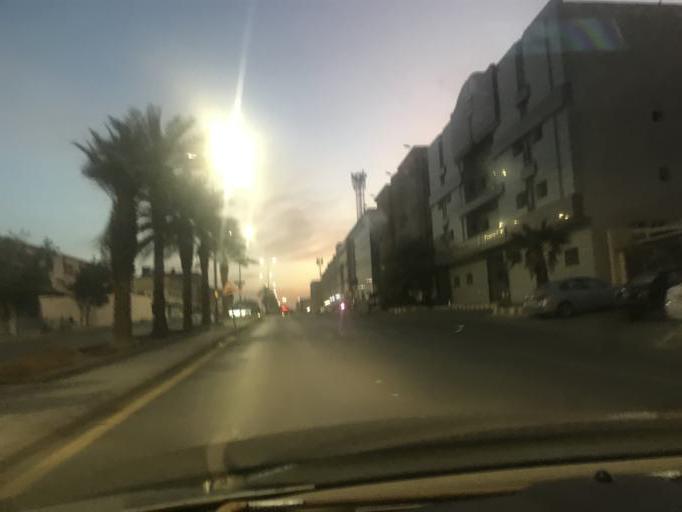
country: SA
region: Ar Riyad
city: Riyadh
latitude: 24.7355
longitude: 46.7602
